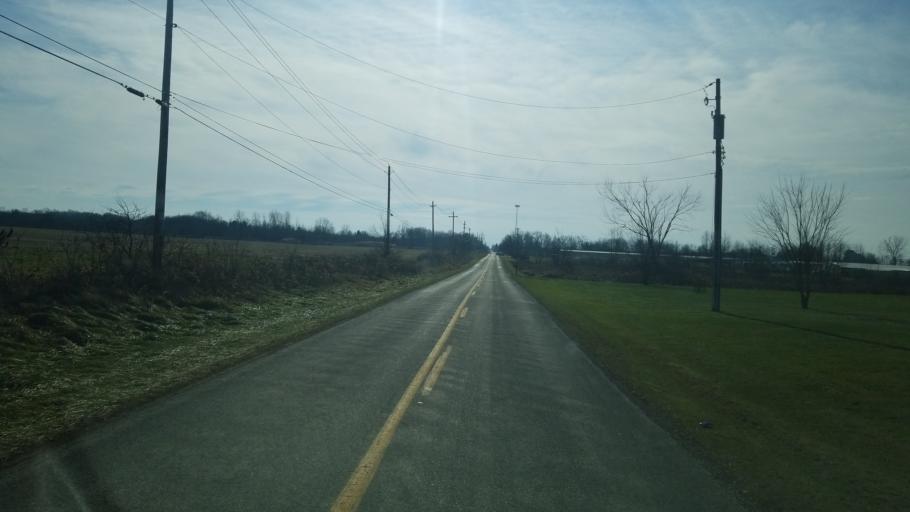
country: US
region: Ohio
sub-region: Ashtabula County
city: Roaming Shores
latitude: 41.6893
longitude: -80.8359
